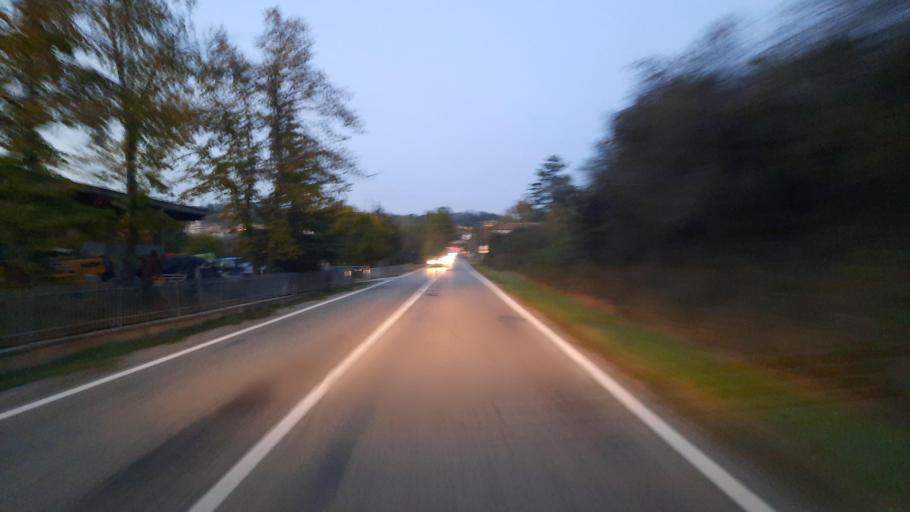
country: IT
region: Piedmont
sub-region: Provincia di Asti
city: Moncalvo
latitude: 45.0378
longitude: 8.2680
